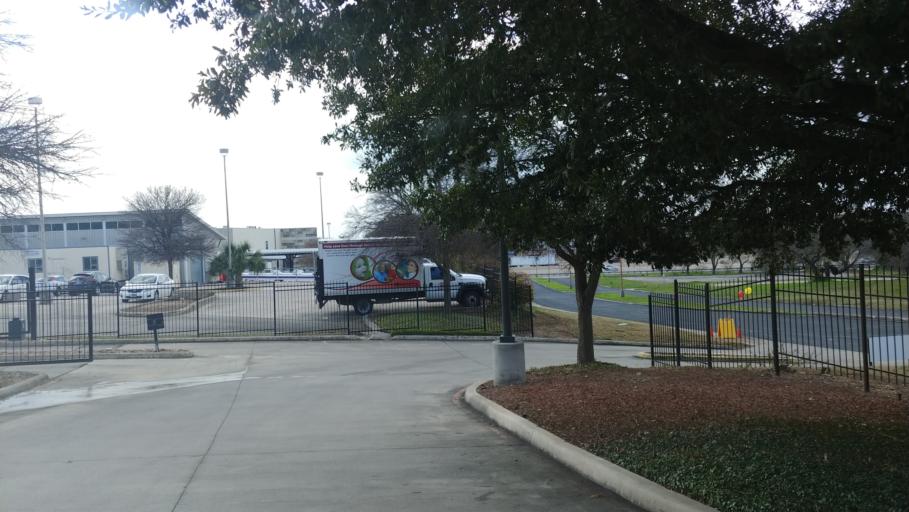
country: US
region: Texas
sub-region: Bexar County
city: Balcones Heights
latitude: 29.4878
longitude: -98.5398
